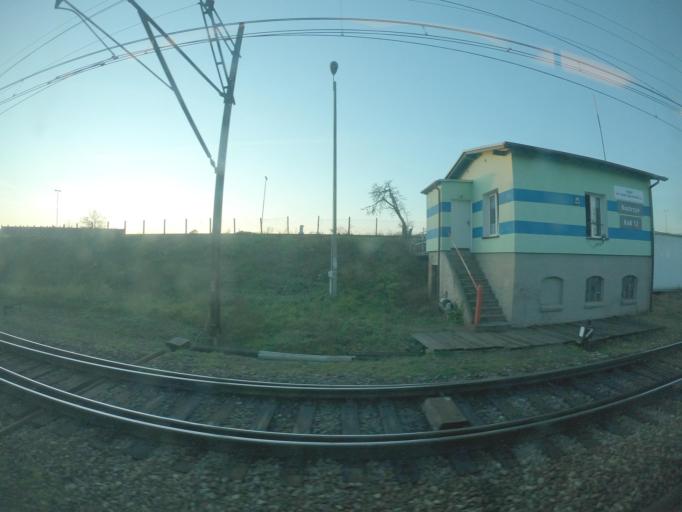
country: PL
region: Lubusz
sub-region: Powiat gorzowski
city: Kostrzyn nad Odra
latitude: 52.5950
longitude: 14.6485
